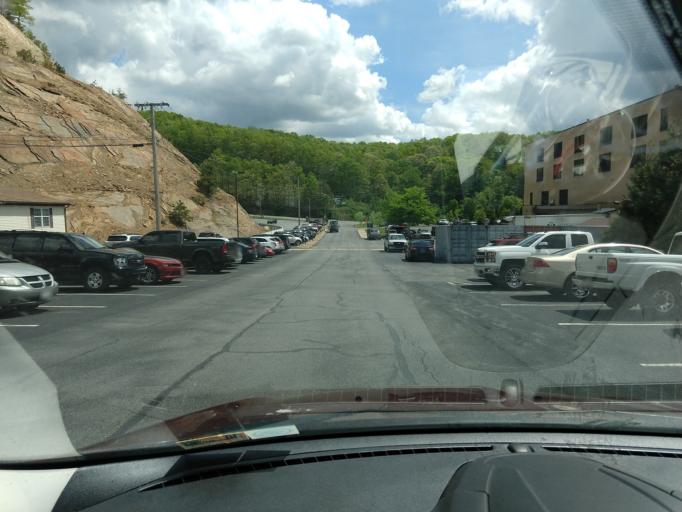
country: US
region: West Virginia
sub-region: Mercer County
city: Bluefield
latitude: 37.2564
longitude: -81.2361
